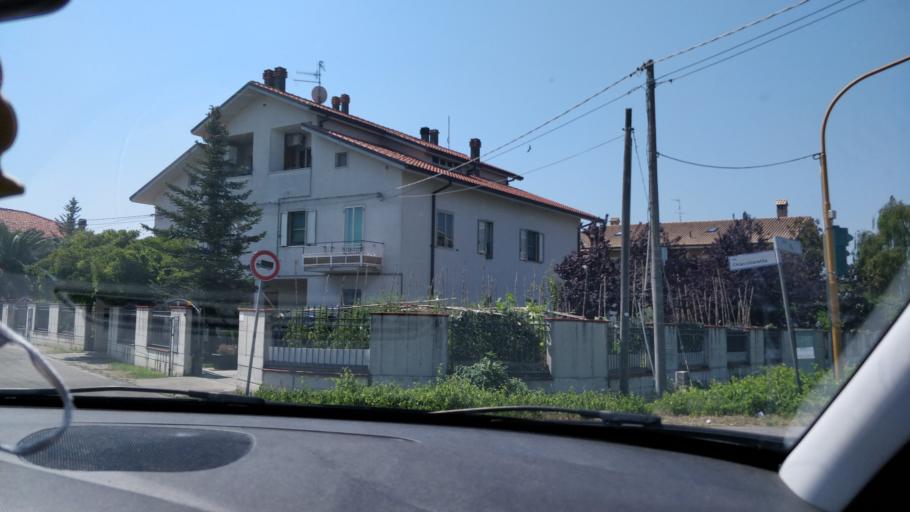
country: IT
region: Abruzzo
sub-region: Provincia di Chieti
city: Sambuceto
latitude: 42.4211
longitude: 14.1765
